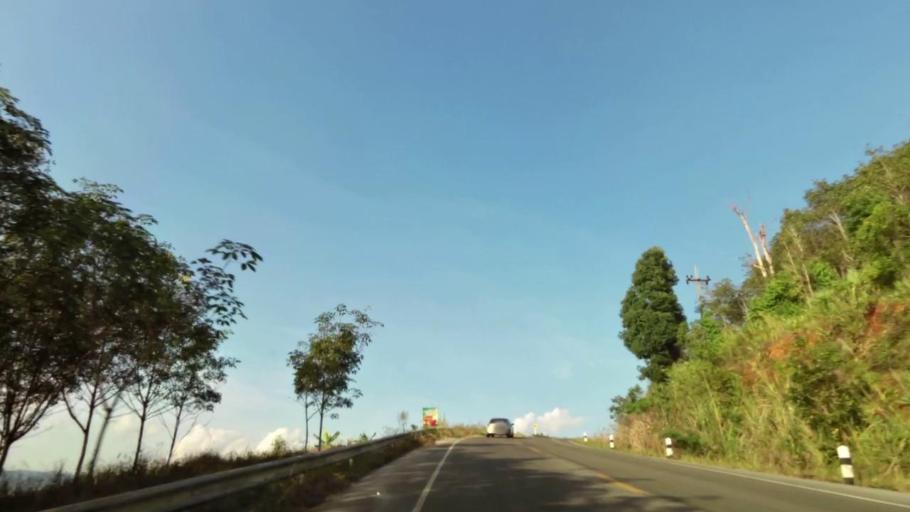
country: TH
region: Chiang Rai
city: Khun Tan
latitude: 19.8652
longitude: 100.4197
